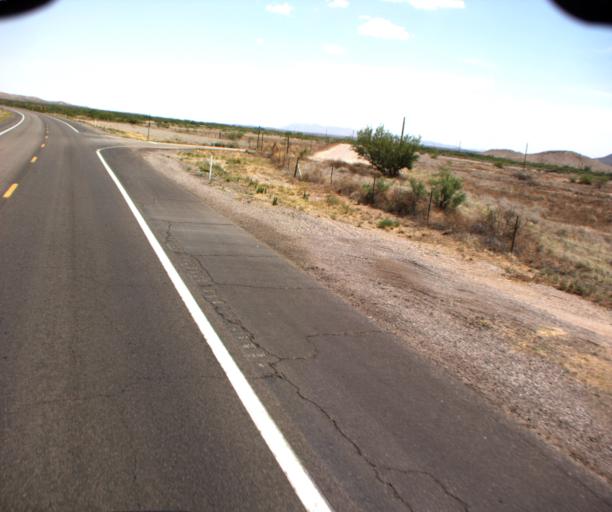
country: US
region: Arizona
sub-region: Greenlee County
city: Clifton
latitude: 32.6646
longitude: -109.0734
